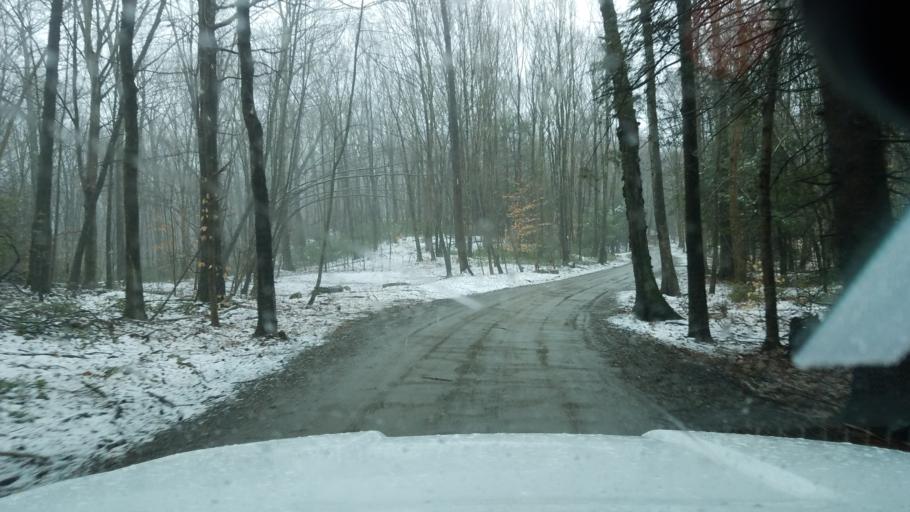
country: US
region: Connecticut
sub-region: New Haven County
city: Heritage Village
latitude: 41.5140
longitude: -73.2838
